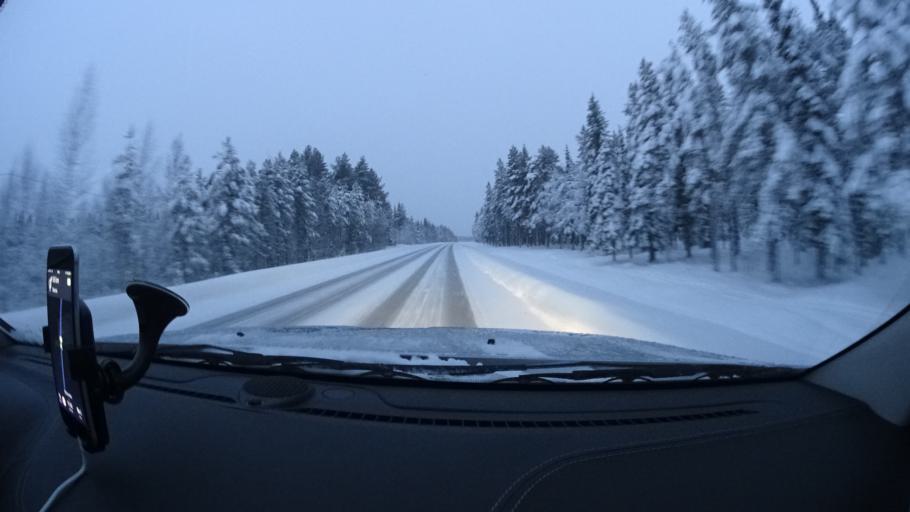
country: FI
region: Lapland
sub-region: Tunturi-Lappi
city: Kittilae
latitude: 67.7266
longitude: 24.8555
